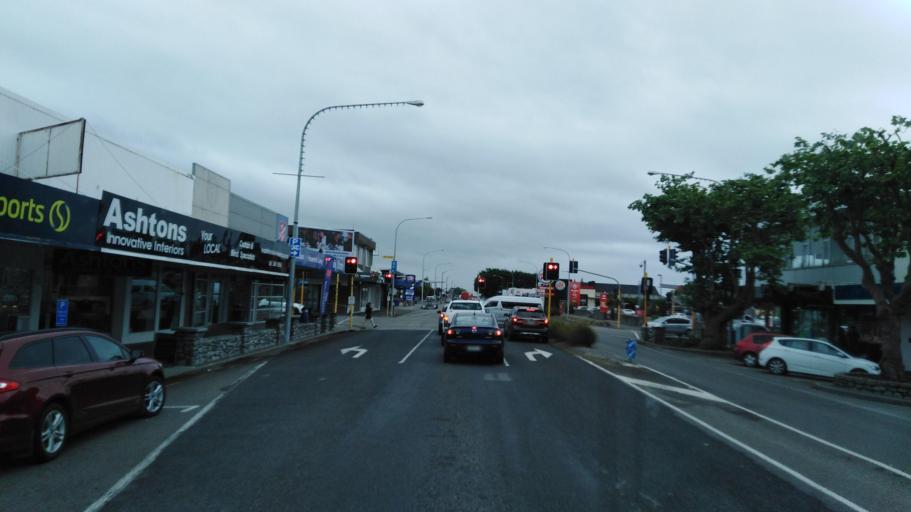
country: NZ
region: Manawatu-Wanganui
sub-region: Horowhenua District
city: Levin
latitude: -40.6233
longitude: 175.2852
